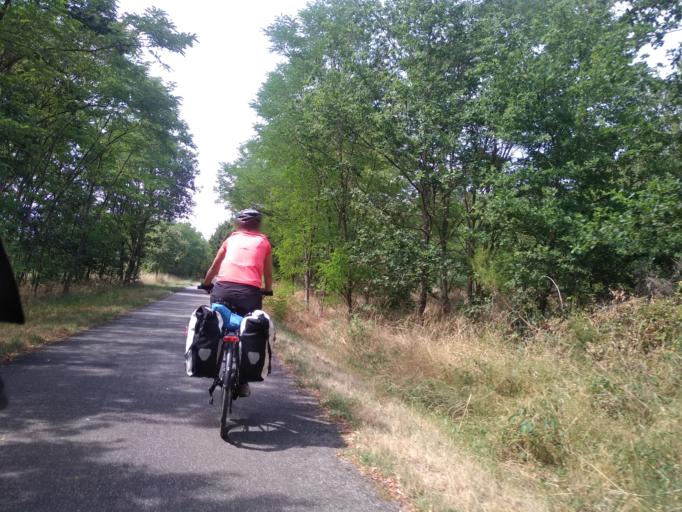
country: FR
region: Auvergne
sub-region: Departement de l'Allier
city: Diou
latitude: 46.5444
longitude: 3.7453
